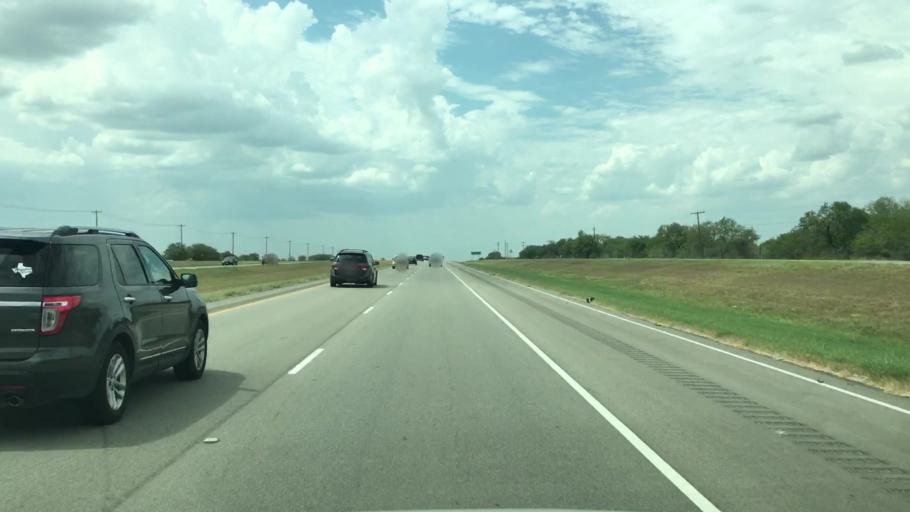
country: US
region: Texas
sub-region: Live Oak County
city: Three Rivers
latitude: 28.4985
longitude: -98.1532
